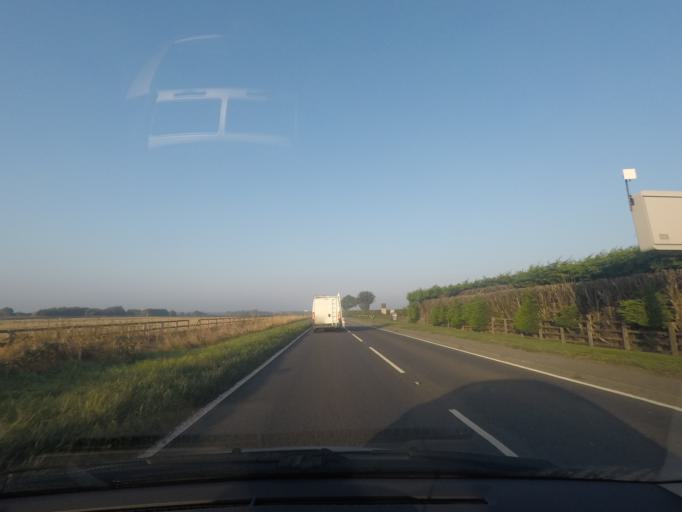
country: GB
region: England
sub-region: City of York
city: Nether Poppleton
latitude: 53.9751
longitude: -1.1613
